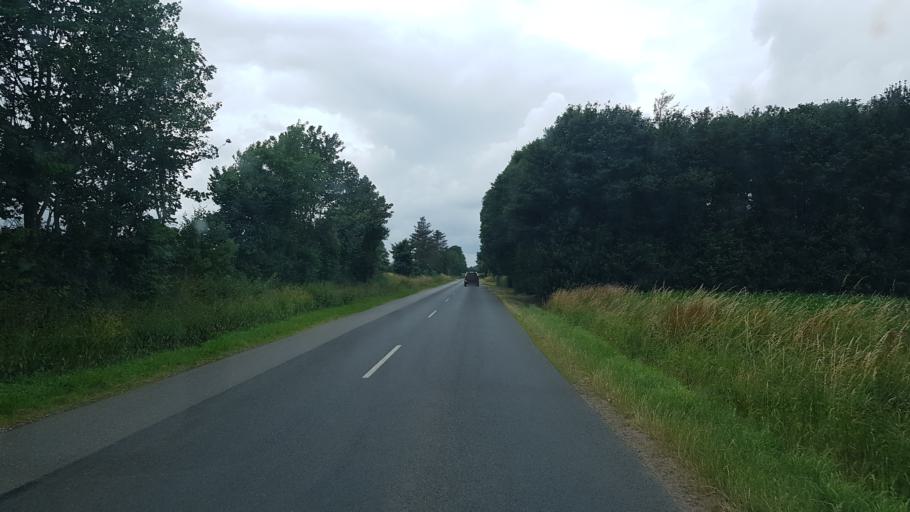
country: DK
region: South Denmark
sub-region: Kolding Kommune
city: Vamdrup
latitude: 55.4319
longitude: 9.2301
